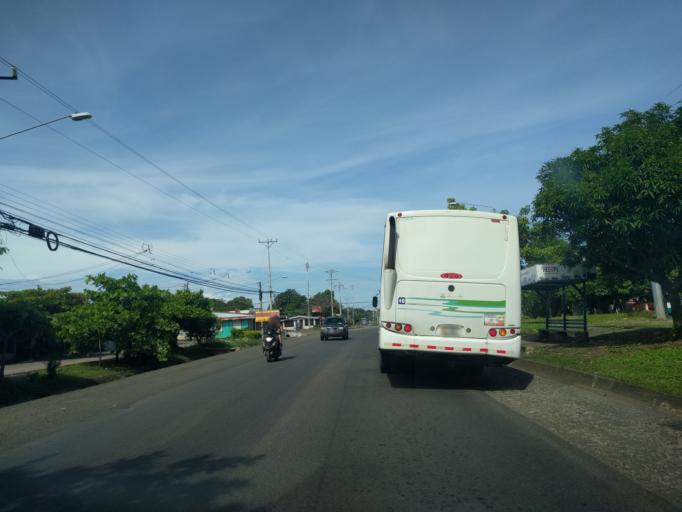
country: CR
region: Puntarenas
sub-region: Canton Central de Puntarenas
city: Chacarita
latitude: 9.9791
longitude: -84.7249
